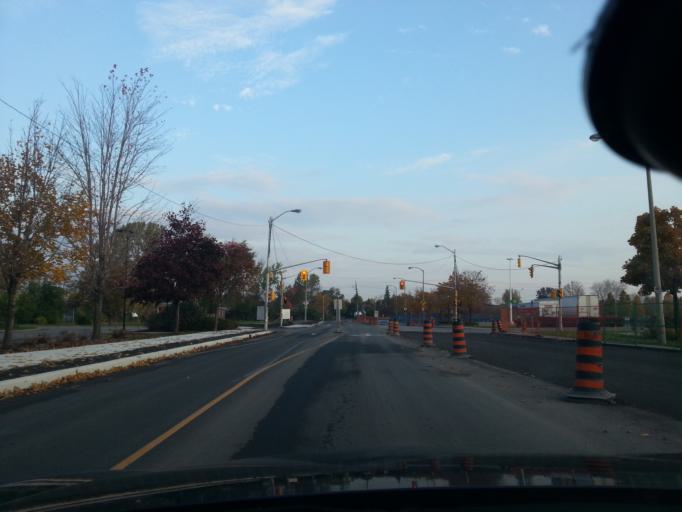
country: CA
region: Ontario
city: Ottawa
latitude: 45.4223
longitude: -75.6423
